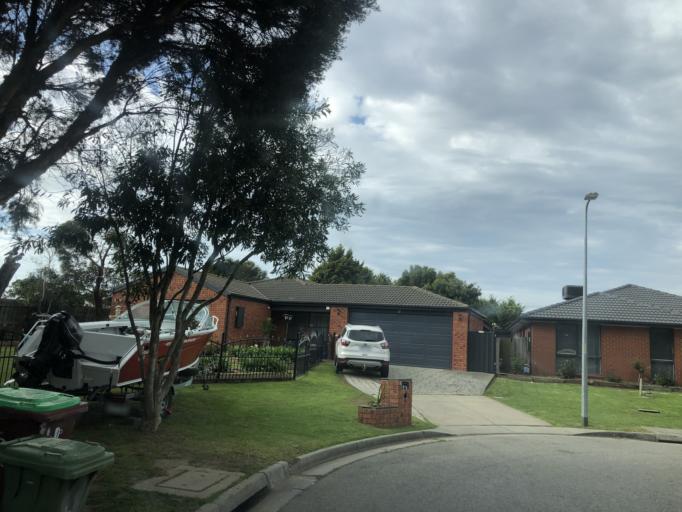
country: AU
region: Victoria
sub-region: Casey
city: Hampton Park
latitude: -38.0214
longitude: 145.2531
